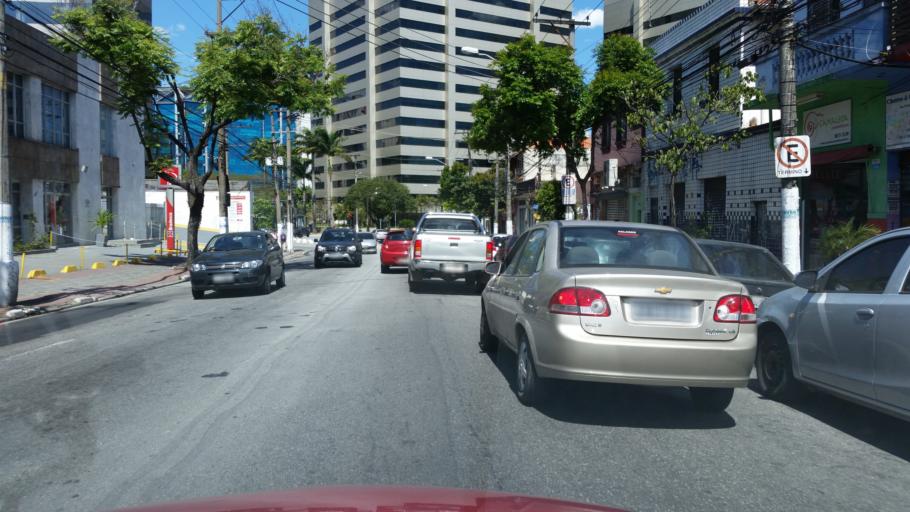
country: BR
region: Sao Paulo
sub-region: Diadema
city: Diadema
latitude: -23.6339
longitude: -46.6435
